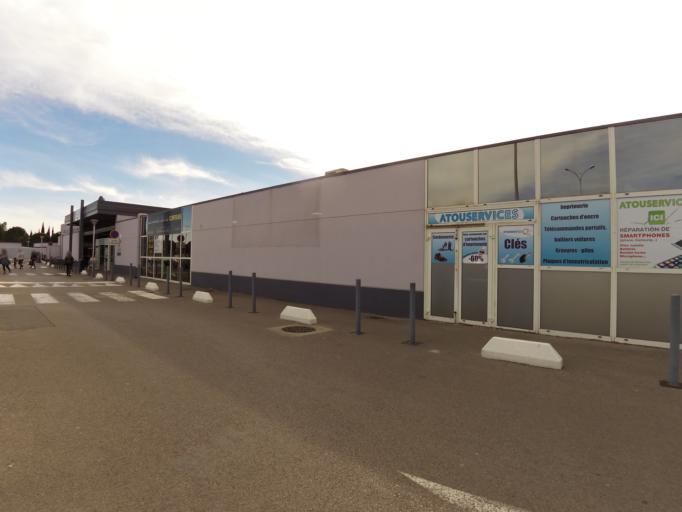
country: FR
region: Languedoc-Roussillon
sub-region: Departement de l'Herault
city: Lunel
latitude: 43.6804
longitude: 4.1476
